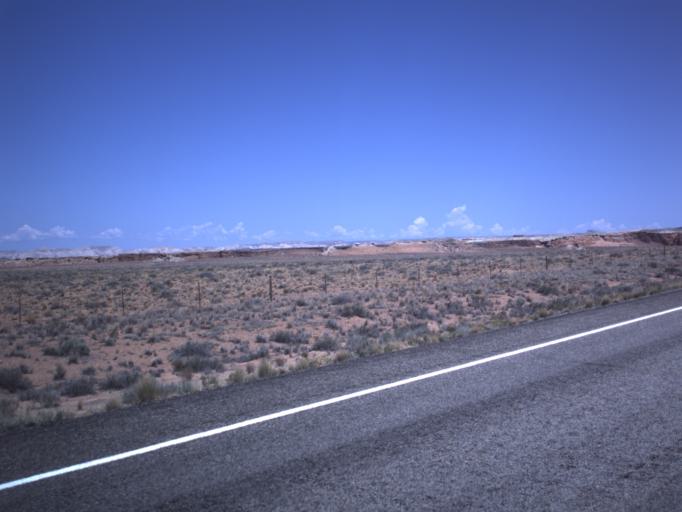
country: US
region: Utah
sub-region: Emery County
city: Ferron
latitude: 38.4183
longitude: -110.6934
